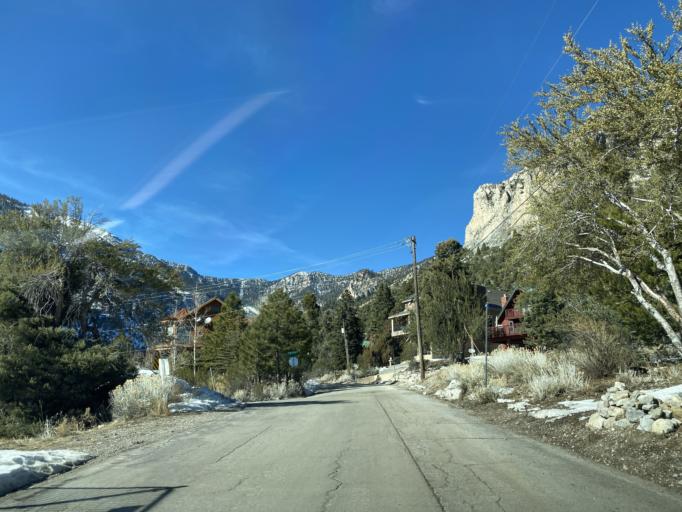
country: US
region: Nevada
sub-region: Nye County
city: Pahrump
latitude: 36.2622
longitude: -115.6509
